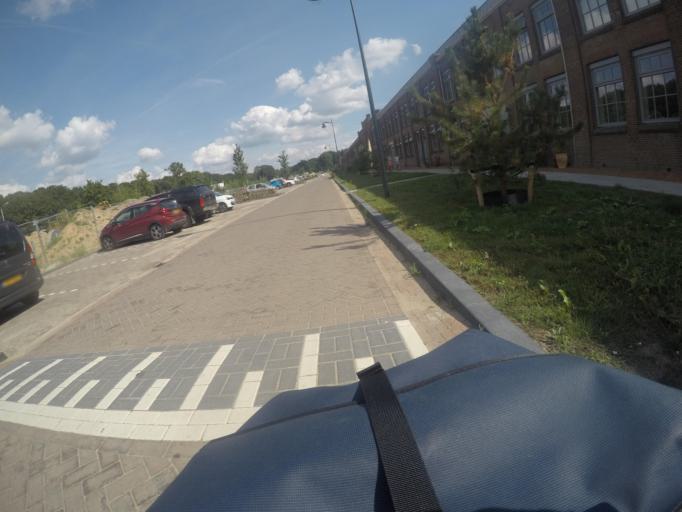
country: NL
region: Gelderland
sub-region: Gemeente Ede
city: Ede
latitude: 52.0255
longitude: 5.6794
